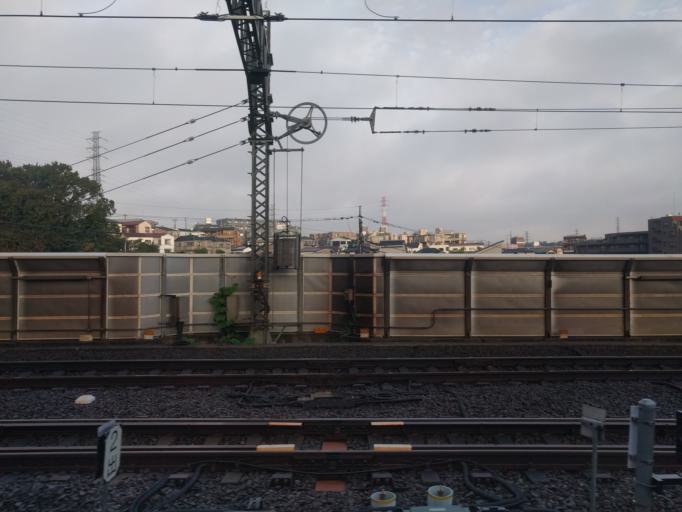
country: JP
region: Tokyo
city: Chofugaoka
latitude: 35.5973
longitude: 139.6079
